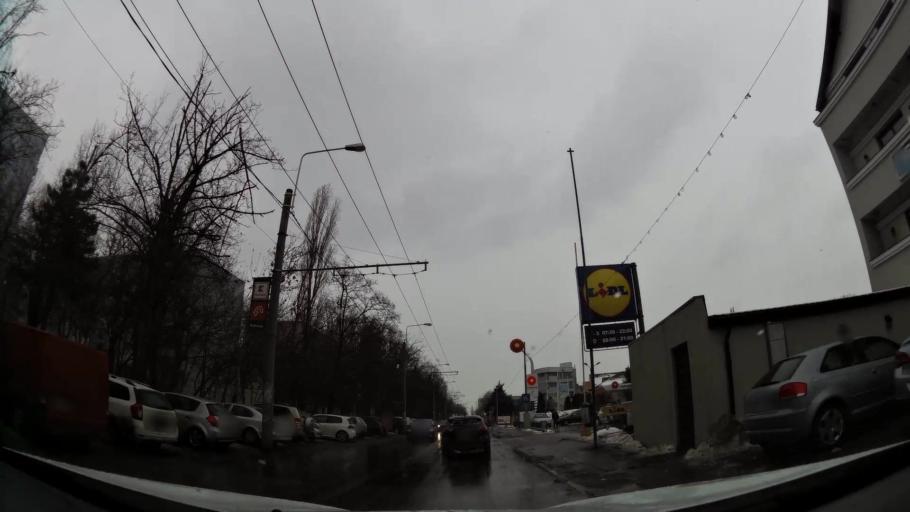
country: RO
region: Ilfov
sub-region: Comuna Chiajna
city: Rosu
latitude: 44.4176
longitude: 26.0137
